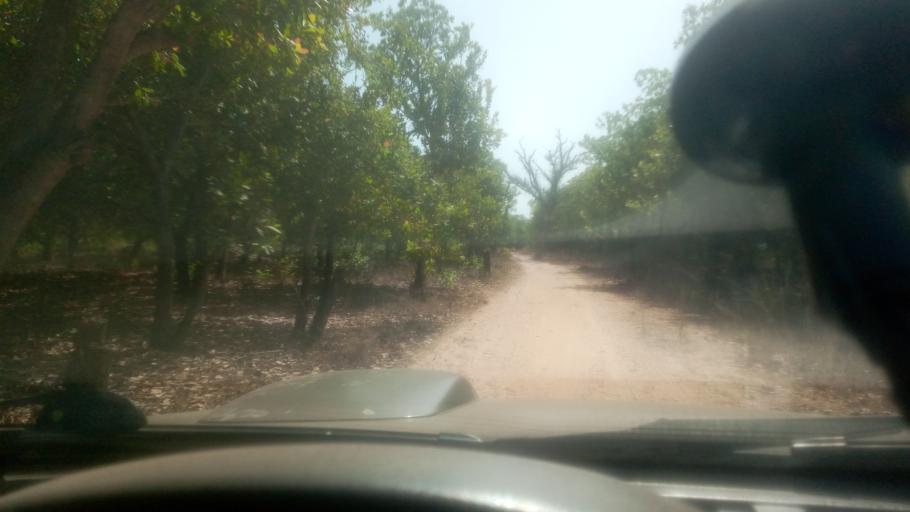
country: GW
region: Oio
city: Farim
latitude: 12.4534
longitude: -15.4195
